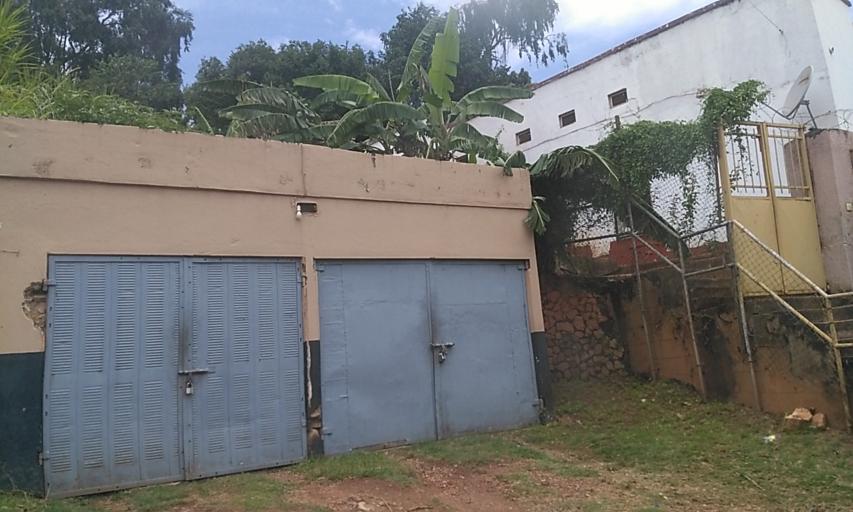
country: UG
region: Central Region
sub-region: Kampala District
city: Kampala
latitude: 0.3313
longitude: 32.5945
